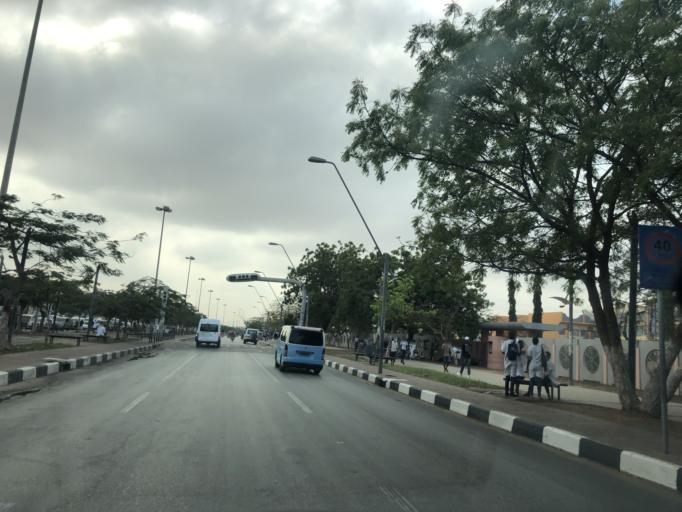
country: AO
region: Luanda
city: Luanda
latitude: -8.8284
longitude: 13.2458
